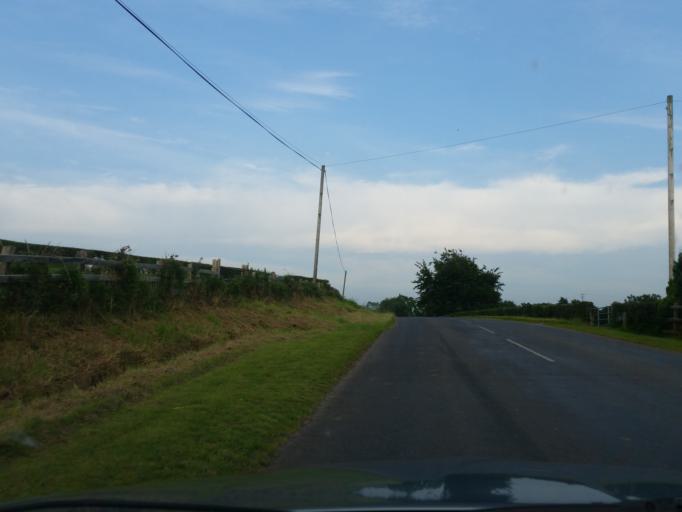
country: GB
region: Northern Ireland
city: Fivemiletown
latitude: 54.3759
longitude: -7.3937
